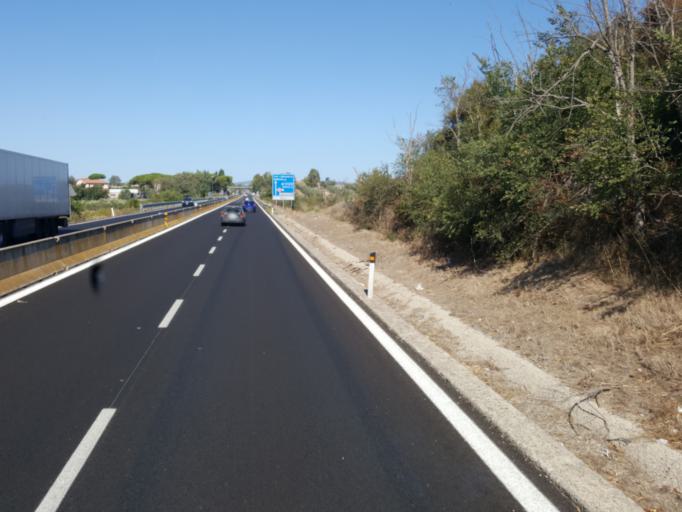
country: IT
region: Latium
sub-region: Provincia di Viterbo
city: Pescia Romana
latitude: 42.4004
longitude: 11.5064
